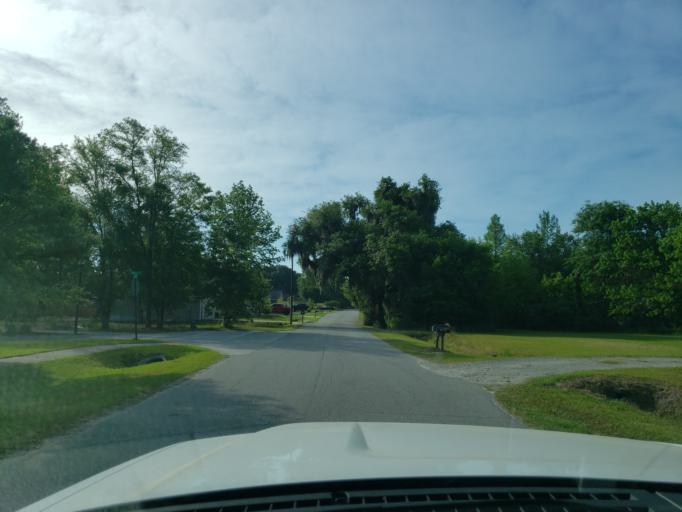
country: US
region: Georgia
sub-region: Chatham County
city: Georgetown
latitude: 32.0048
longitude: -81.2294
